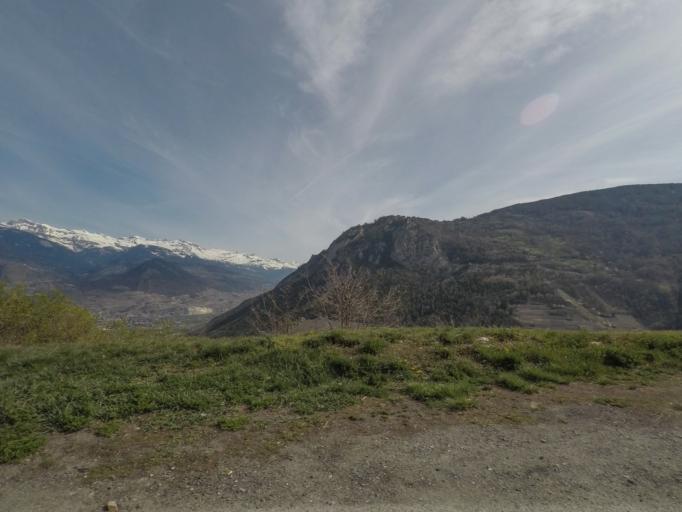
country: CH
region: Valais
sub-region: Herens District
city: Vex
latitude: 46.2194
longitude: 7.4028
